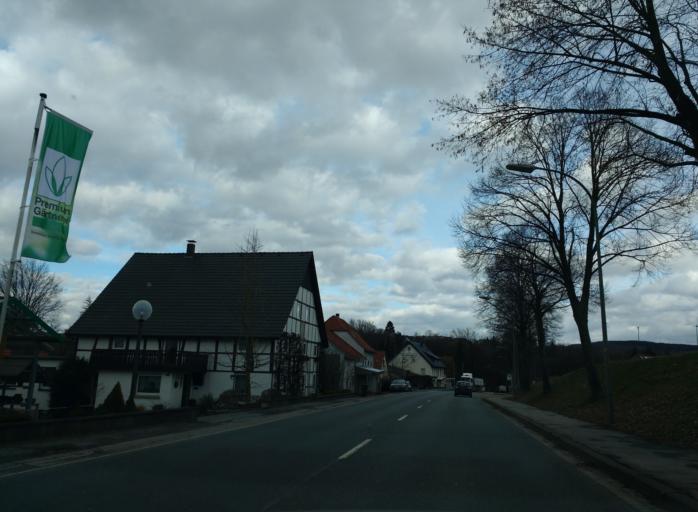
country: DE
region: North Rhine-Westphalia
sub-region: Regierungsbezirk Detmold
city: Lemgo
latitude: 52.1032
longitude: 8.9351
